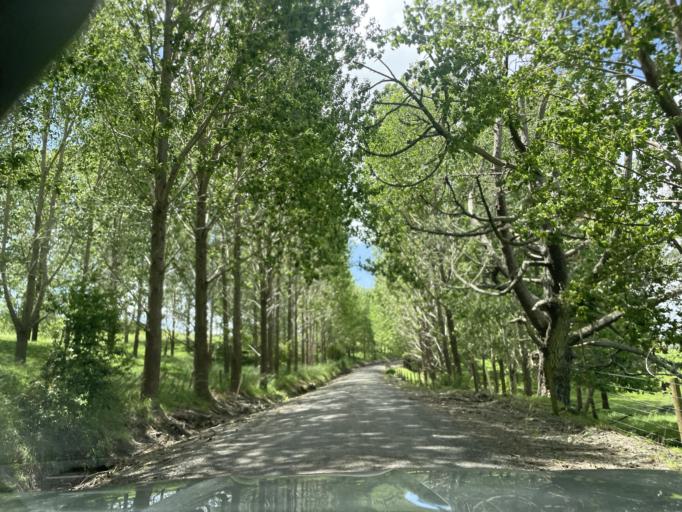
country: NZ
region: Auckland
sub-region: Auckland
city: Wellsford
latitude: -36.1759
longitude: 174.3153
